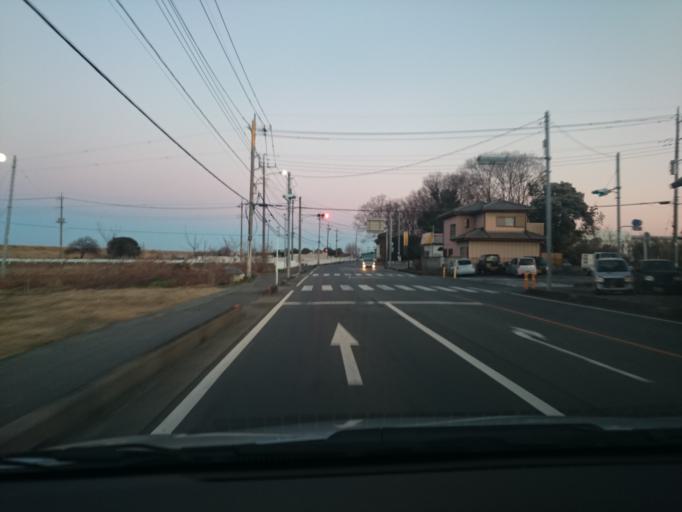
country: JP
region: Saitama
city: Fukayacho
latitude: 36.2290
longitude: 139.3150
